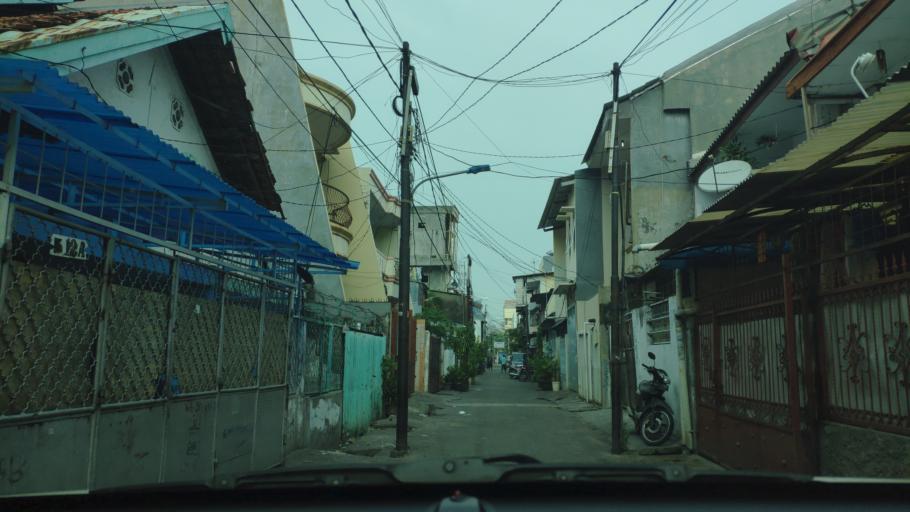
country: ID
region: Jakarta Raya
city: Jakarta
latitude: -6.1588
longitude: 106.8130
